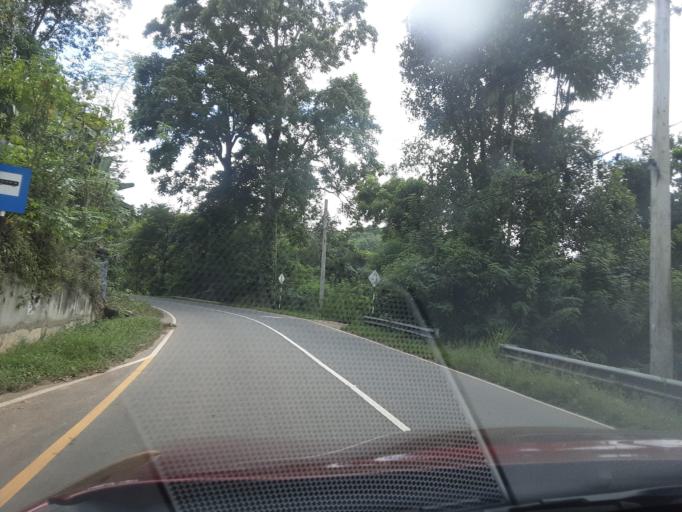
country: LK
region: Uva
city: Monaragala
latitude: 6.8985
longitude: 81.2496
